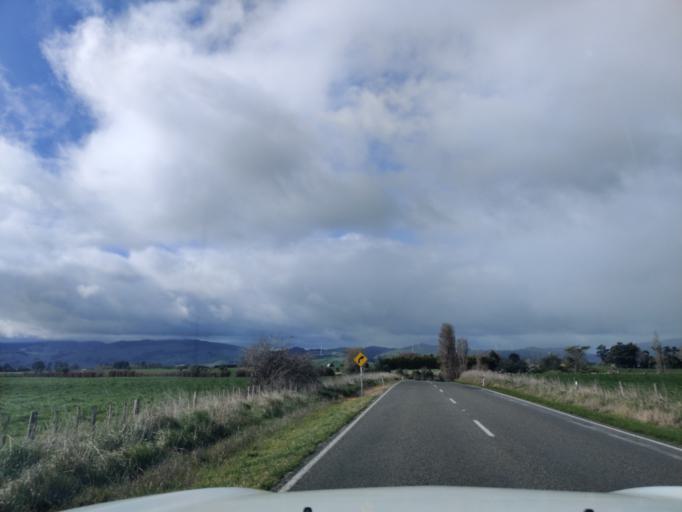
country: NZ
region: Manawatu-Wanganui
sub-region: Palmerston North City
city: Palmerston North
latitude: -40.2910
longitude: 175.7249
